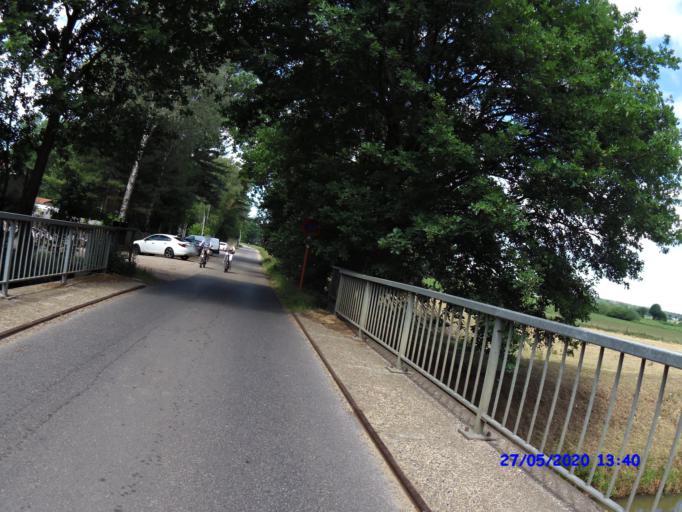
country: BE
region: Flanders
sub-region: Provincie Antwerpen
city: Kasterlee
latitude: 51.2096
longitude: 4.9389
